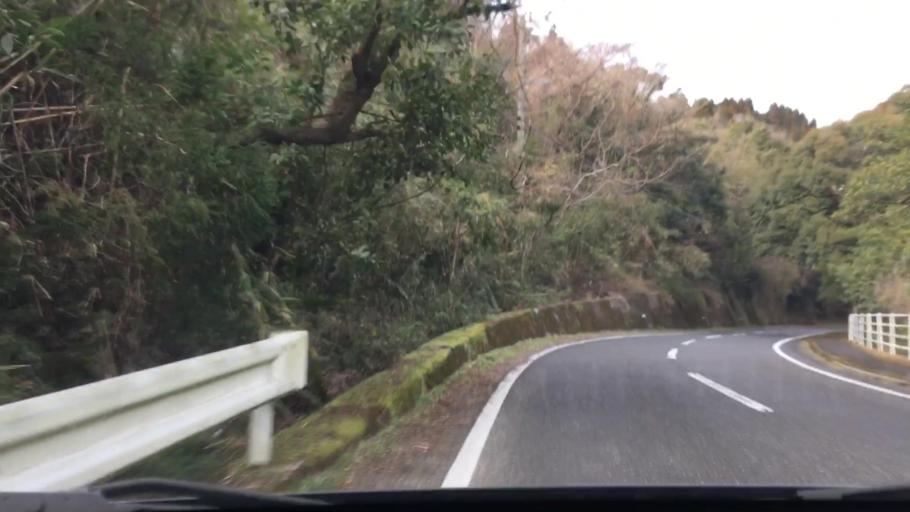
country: JP
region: Miyazaki
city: Kushima
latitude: 31.5419
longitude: 131.2421
